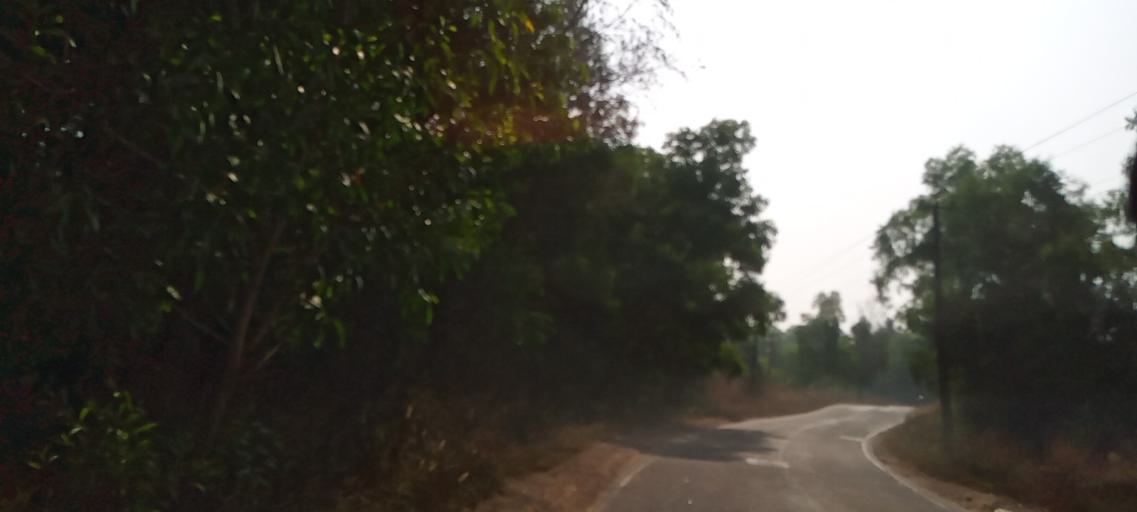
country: IN
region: Karnataka
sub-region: Udupi
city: Coondapoor
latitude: 13.5168
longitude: 74.7649
